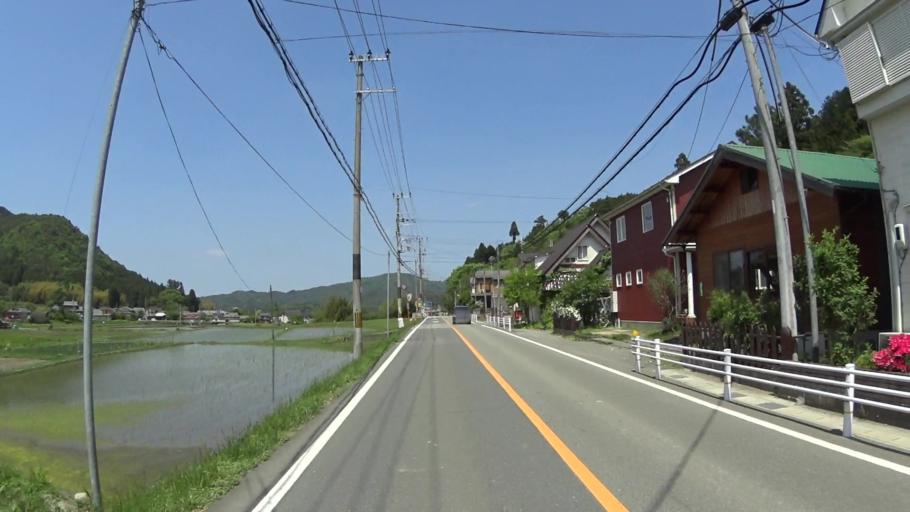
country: JP
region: Kyoto
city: Kameoka
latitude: 35.0093
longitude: 135.4844
